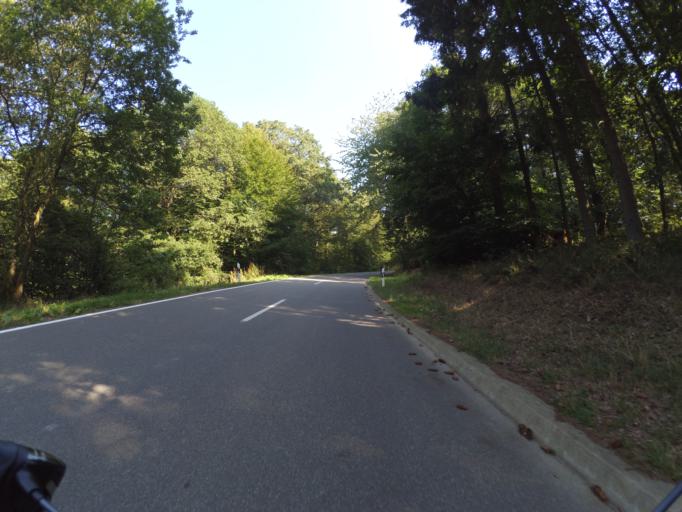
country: DE
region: Rheinland-Pfalz
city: Wintrich
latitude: 49.8612
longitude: 6.9738
